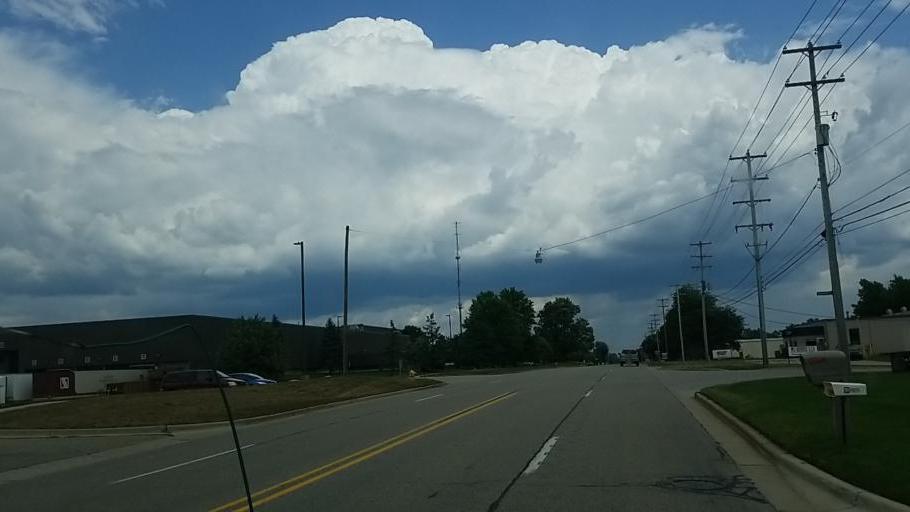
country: US
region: Michigan
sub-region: Kent County
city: Walker
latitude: 43.0155
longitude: -85.7470
